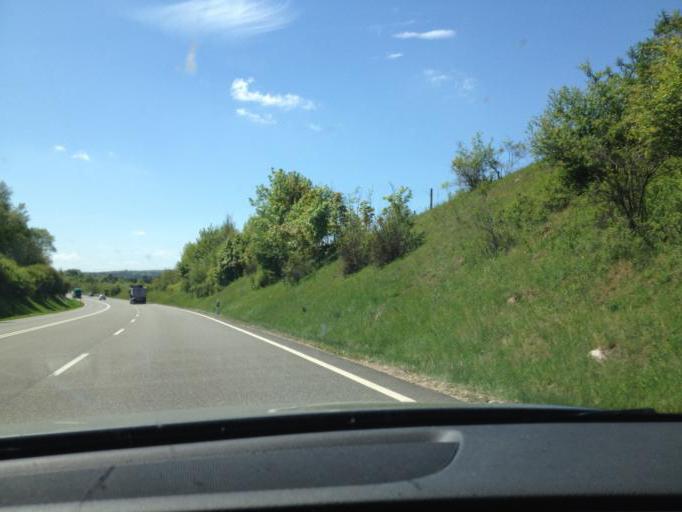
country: DE
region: North Rhine-Westphalia
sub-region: Regierungsbezirk Koln
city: Blankenheim
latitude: 50.4492
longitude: 6.6260
